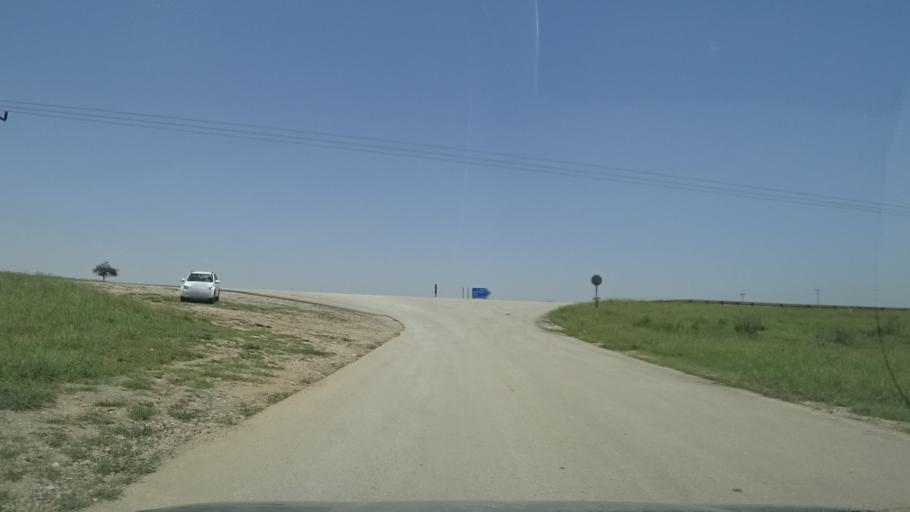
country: OM
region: Zufar
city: Salalah
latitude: 17.2504
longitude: 54.2760
